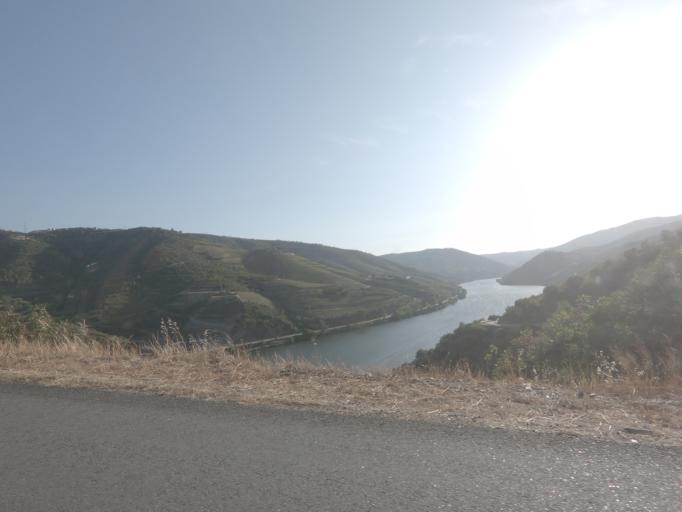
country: PT
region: Viseu
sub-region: Tabuaco
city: Tabuaco
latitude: 41.1615
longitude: -7.6030
